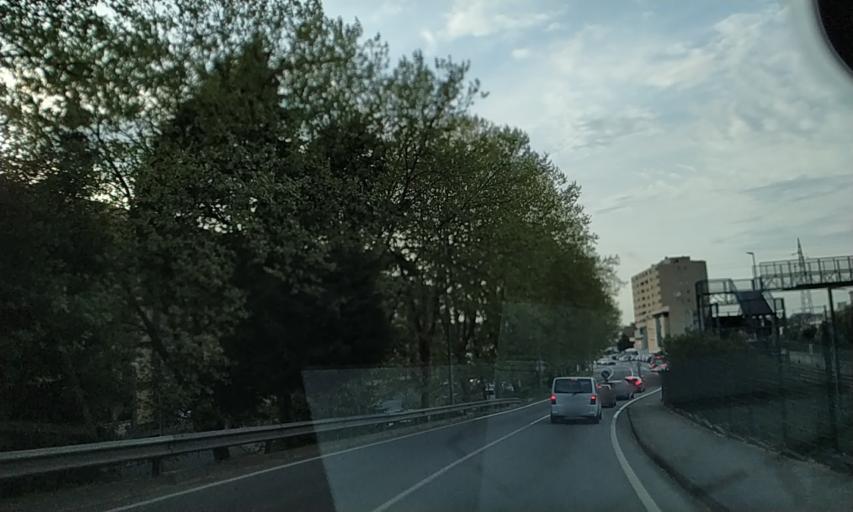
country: PT
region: Porto
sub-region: Valongo
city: Campo
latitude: 41.1827
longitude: -8.4823
